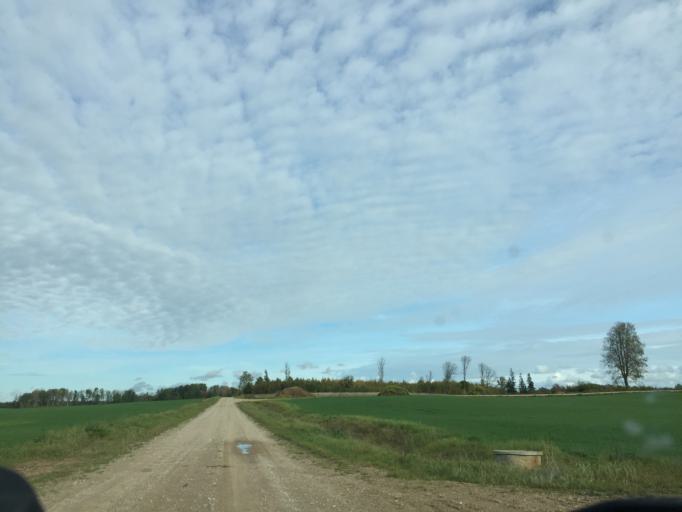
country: LV
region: Jaunpils
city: Jaunpils
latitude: 56.6299
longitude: 23.0650
